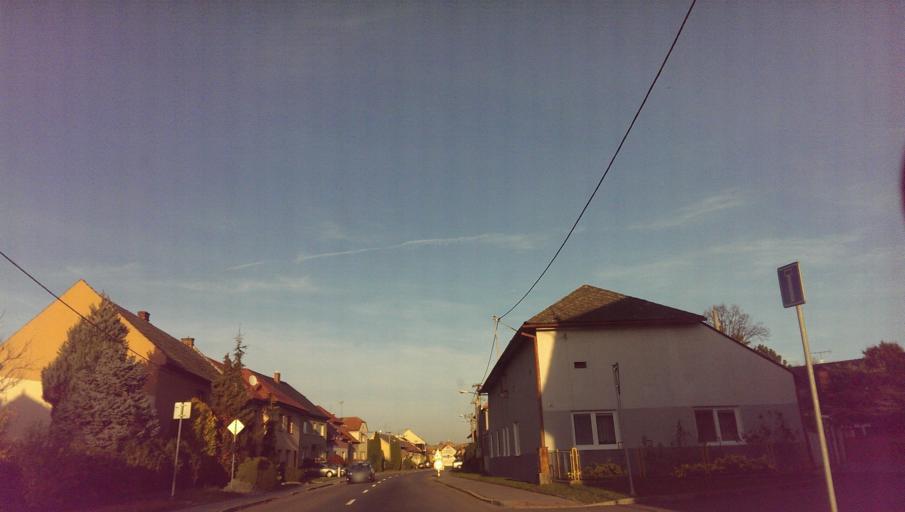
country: CZ
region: Zlin
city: Bilovice
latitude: 49.0995
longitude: 17.5503
